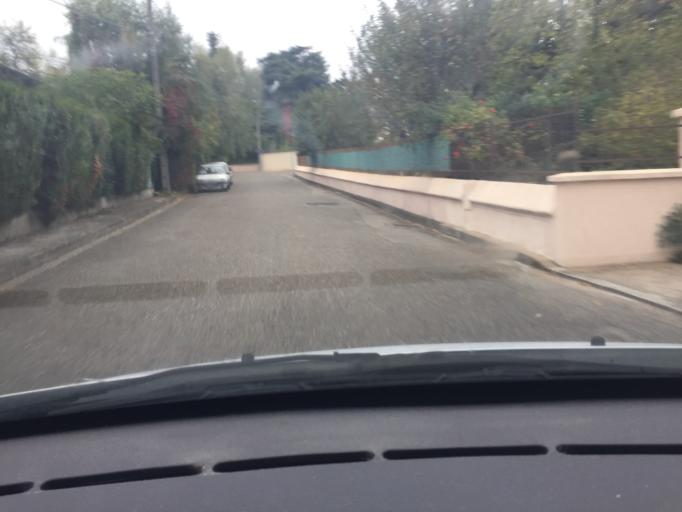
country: FR
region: Rhone-Alpes
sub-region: Departement du Rhone
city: Sathonay-Camp
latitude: 45.8055
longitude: 4.8806
